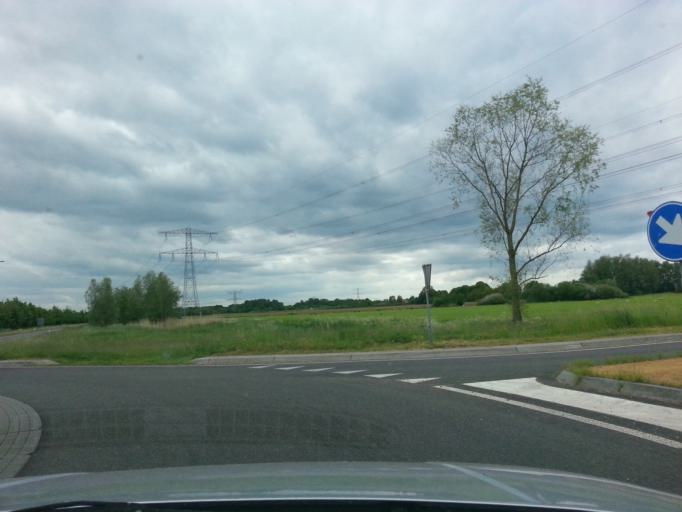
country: NL
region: Gelderland
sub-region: Gemeente Zutphen
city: Leesten
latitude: 52.1340
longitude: 6.2585
